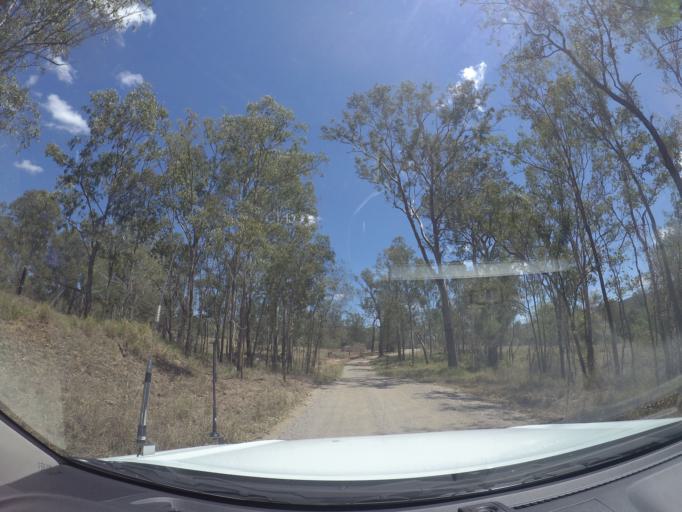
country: AU
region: Queensland
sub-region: Logan
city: North Maclean
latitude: -27.8332
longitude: 152.8680
